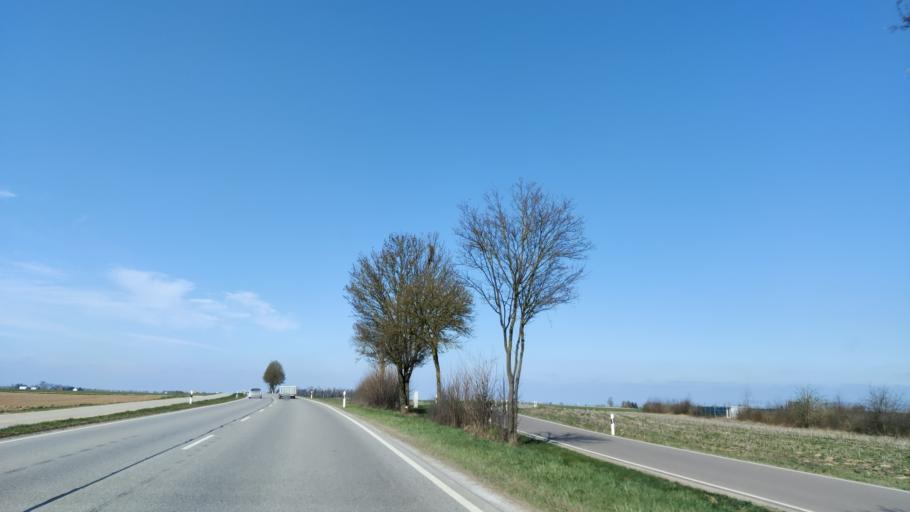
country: DE
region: Bavaria
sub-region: Lower Bavaria
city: Strasskirchen
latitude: 48.8381
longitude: 12.7017
